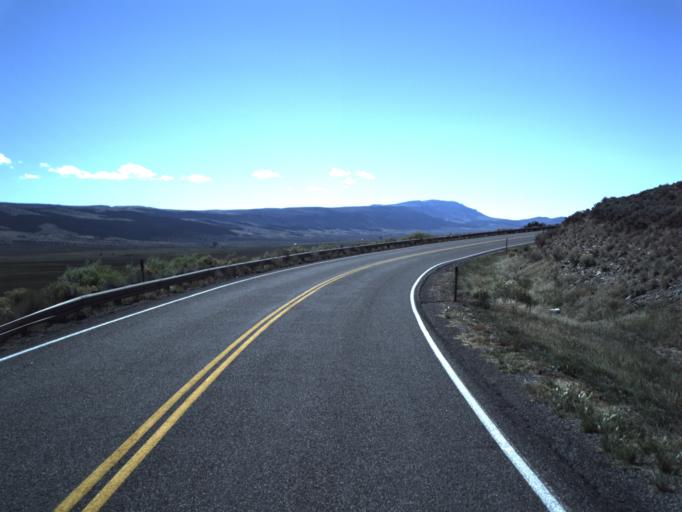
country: US
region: Utah
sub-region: Sevier County
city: Monroe
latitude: 38.5507
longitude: -111.8665
